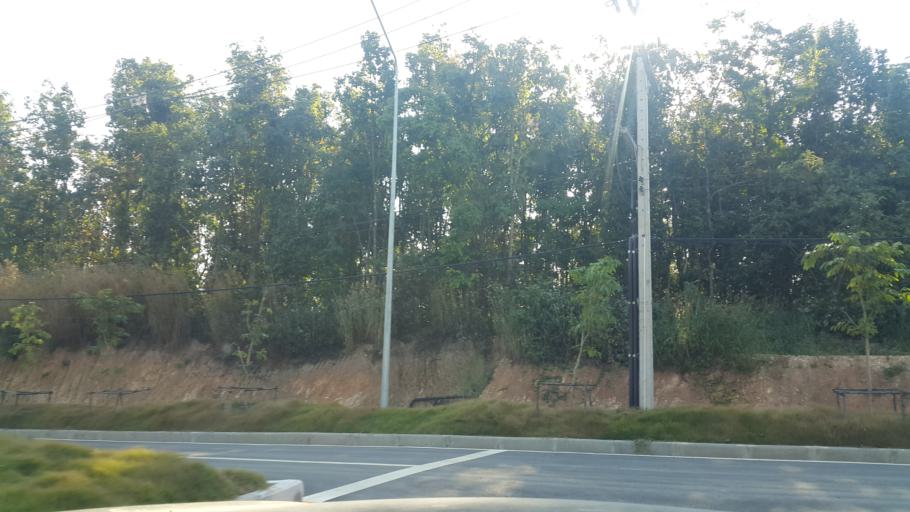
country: TH
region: Lamphun
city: Mae Tha
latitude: 18.5113
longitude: 99.1153
